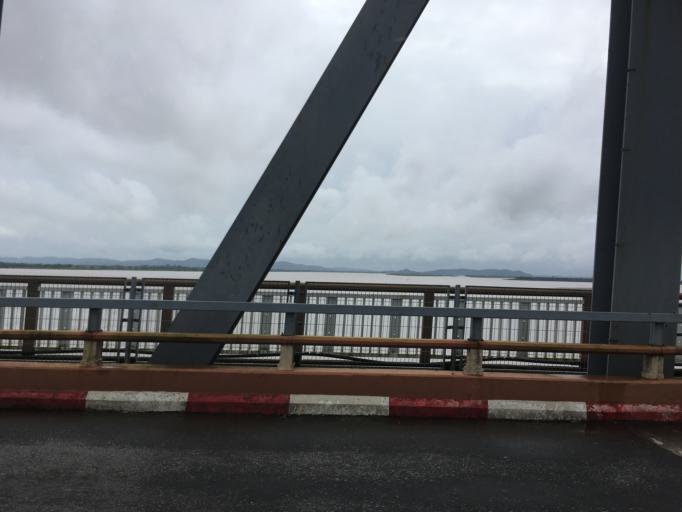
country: MM
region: Mon
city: Mawlamyine
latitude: 16.5071
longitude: 97.6198
